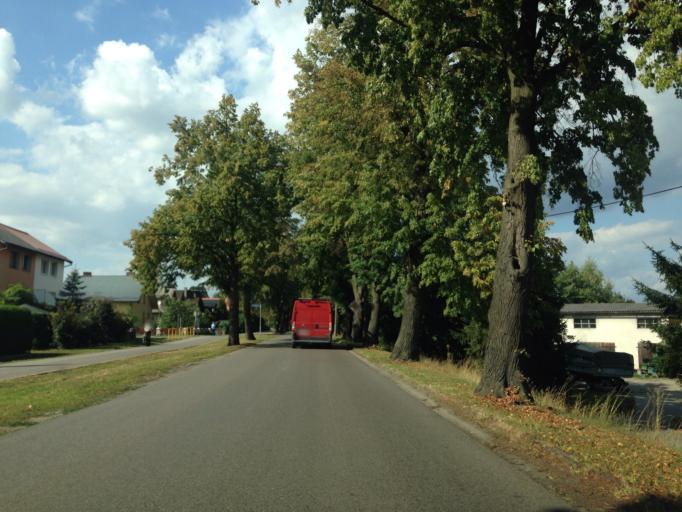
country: PL
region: Warmian-Masurian Voivodeship
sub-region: Powiat ilawski
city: Ilawa
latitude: 53.6129
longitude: 19.5695
